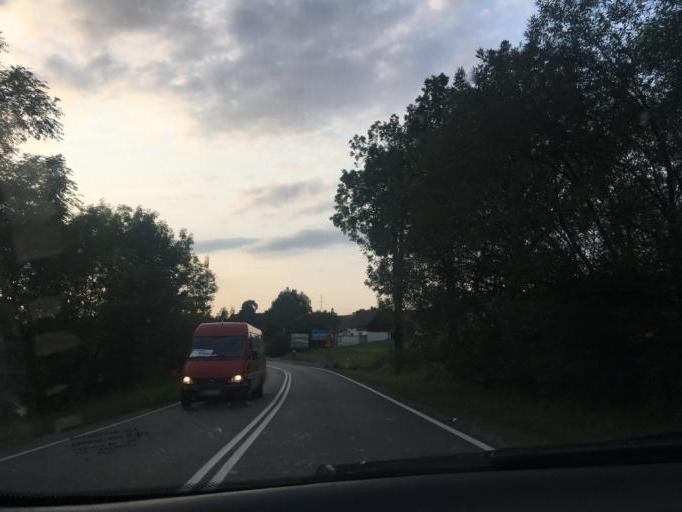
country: PL
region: Lower Silesian Voivodeship
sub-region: Powiat klodzki
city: Bozkow
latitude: 50.5351
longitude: 16.5791
